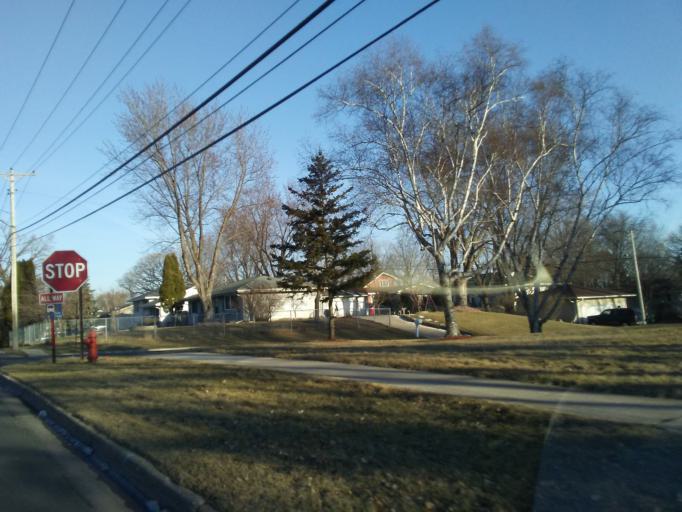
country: US
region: Minnesota
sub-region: Hennepin County
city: Edina
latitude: 44.8516
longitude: -93.3389
